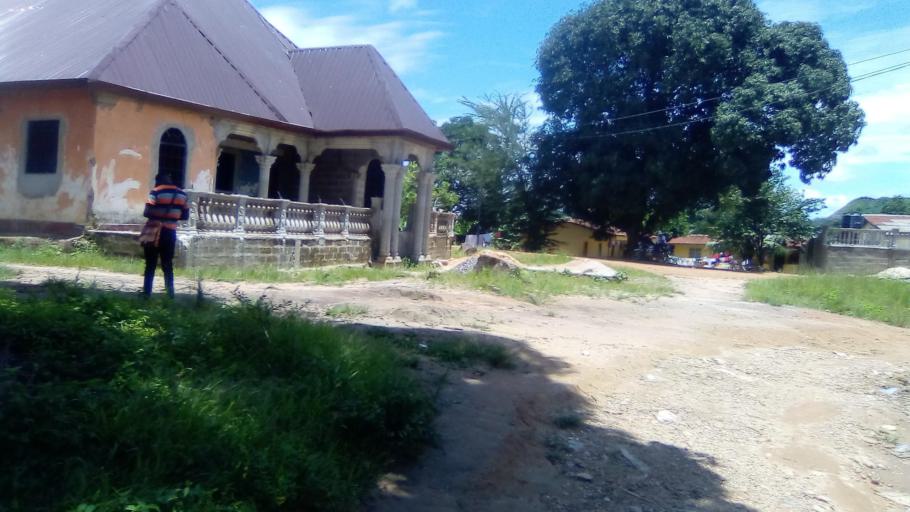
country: SL
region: Eastern Province
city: Koidu
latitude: 8.6321
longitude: -10.9888
